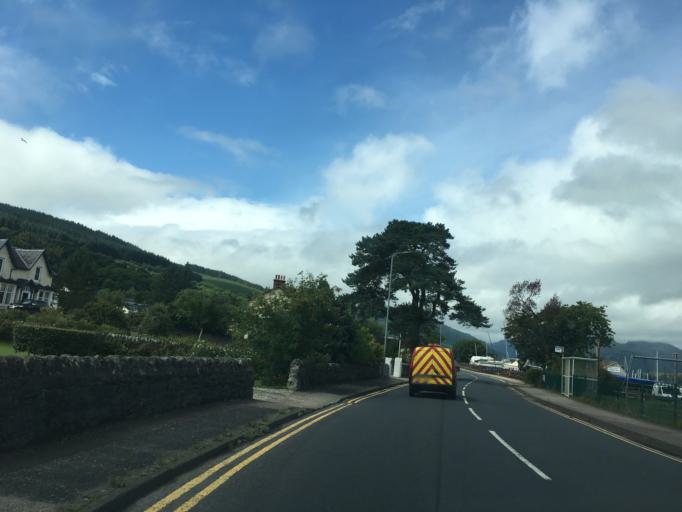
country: GB
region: Scotland
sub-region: Argyll and Bute
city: Dunoon
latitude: 55.9807
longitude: -4.9445
